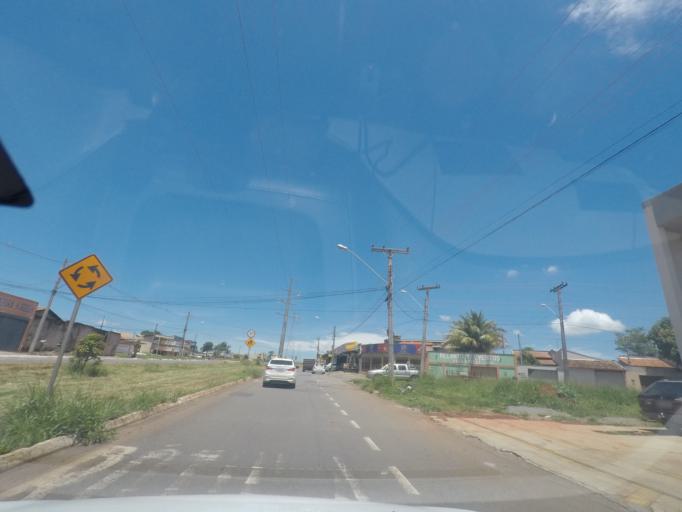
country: BR
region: Goias
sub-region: Goiania
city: Goiania
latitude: -16.7337
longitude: -49.3578
